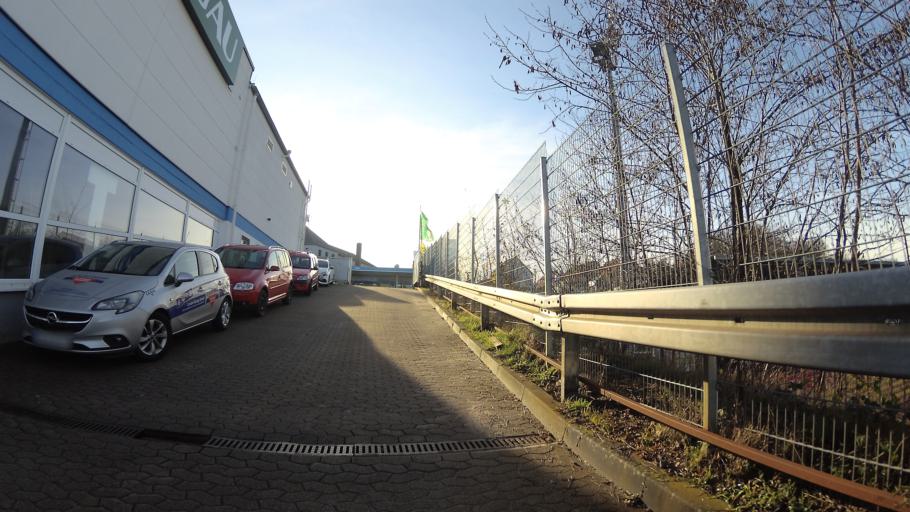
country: DE
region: Saarland
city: Spiesen-Elversberg
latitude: 49.3182
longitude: 7.1224
